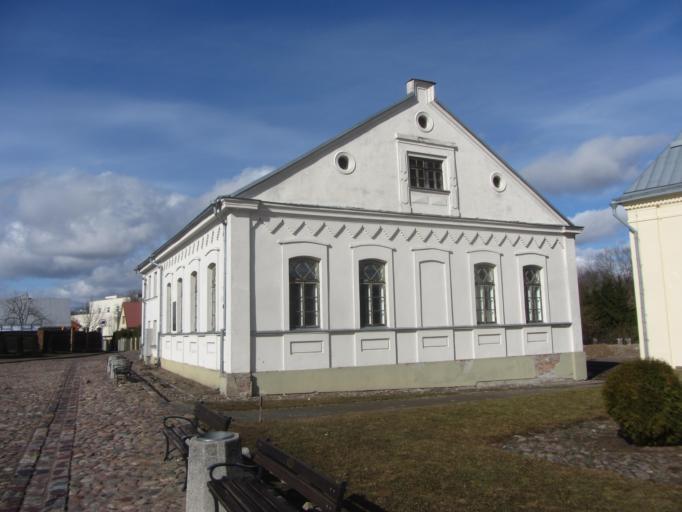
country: LT
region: Kauno apskritis
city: Kedainiai
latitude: 55.2876
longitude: 23.9813
